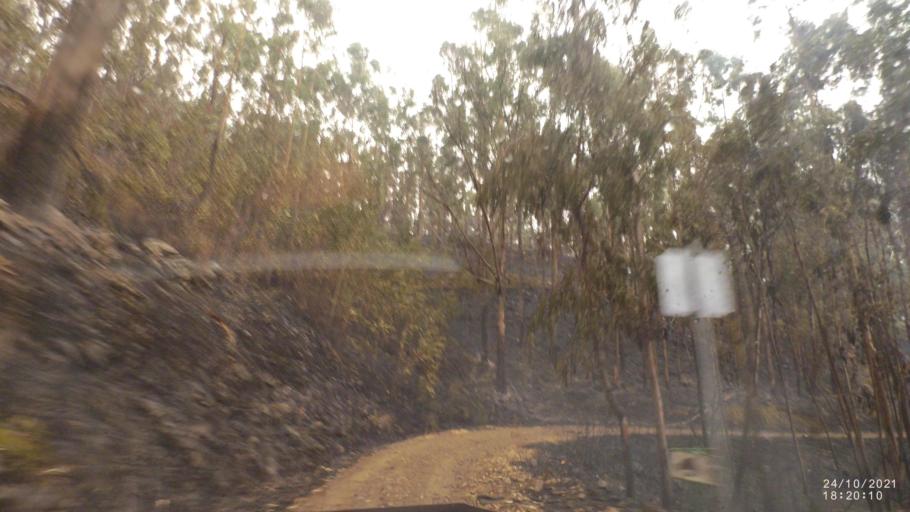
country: BO
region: Cochabamba
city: Cochabamba
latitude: -17.3320
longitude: -66.1406
